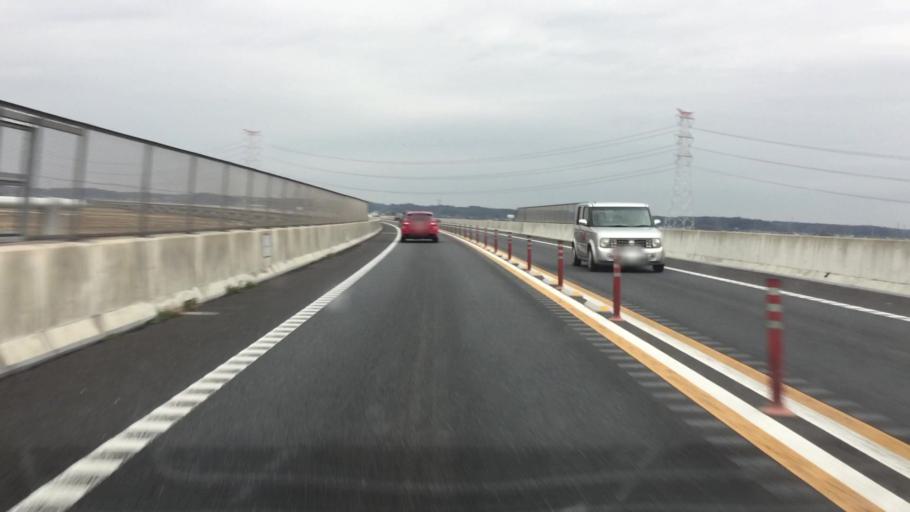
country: JP
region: Ibaraki
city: Inashiki
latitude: 35.9092
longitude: 140.3709
